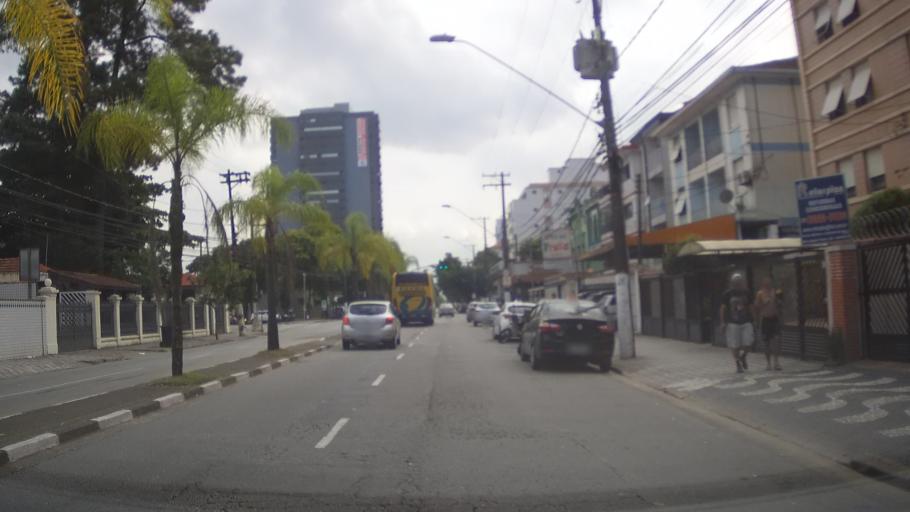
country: BR
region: Sao Paulo
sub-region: Santos
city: Santos
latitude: -23.9569
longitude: -46.3241
